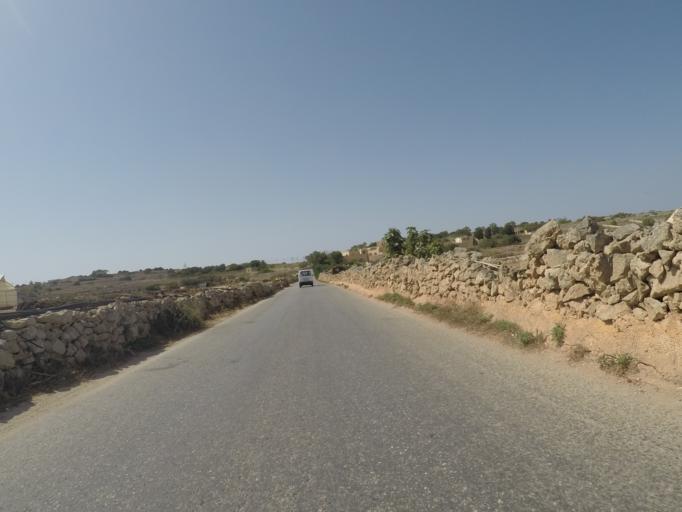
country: MT
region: L-Imgarr
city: Imgarr
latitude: 35.9253
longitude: 14.3788
